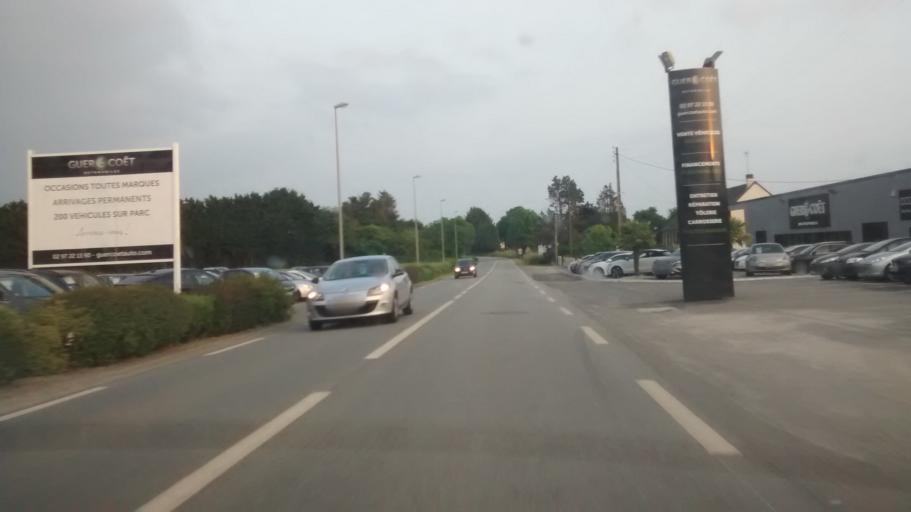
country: FR
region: Brittany
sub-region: Departement du Morbihan
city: Guer
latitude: 47.9268
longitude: -2.1267
